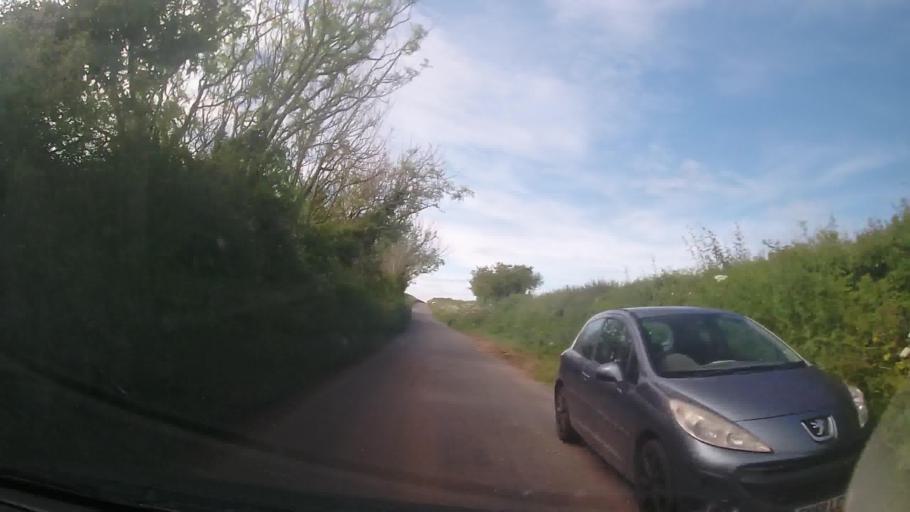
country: GB
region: England
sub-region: Devon
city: Salcombe
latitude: 50.2440
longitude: -3.6806
